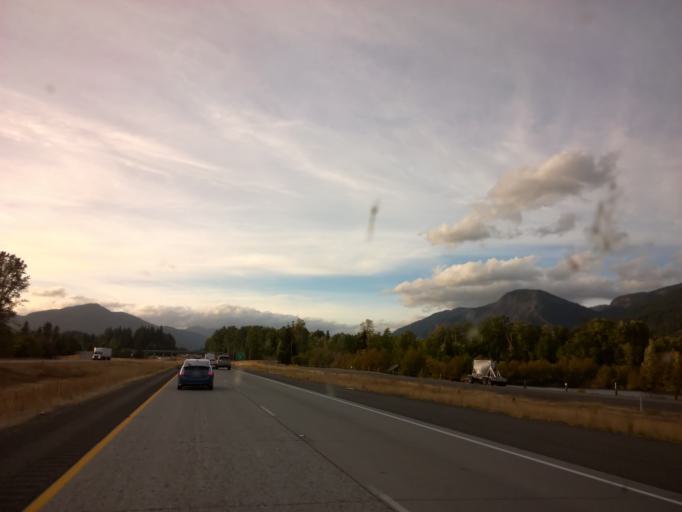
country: US
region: Washington
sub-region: Kittitas County
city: Cle Elum
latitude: 47.2328
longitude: -121.1693
